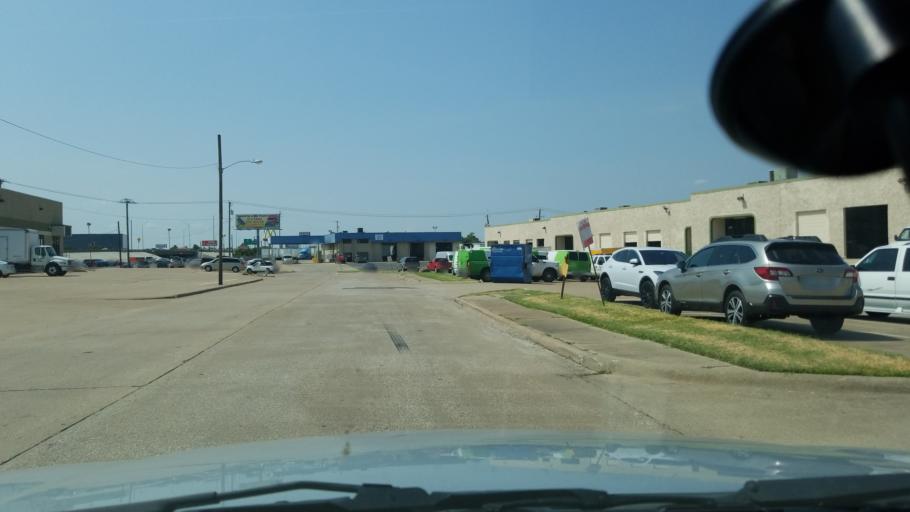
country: US
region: Texas
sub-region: Dallas County
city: Farmers Branch
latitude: 32.8677
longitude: -96.9004
